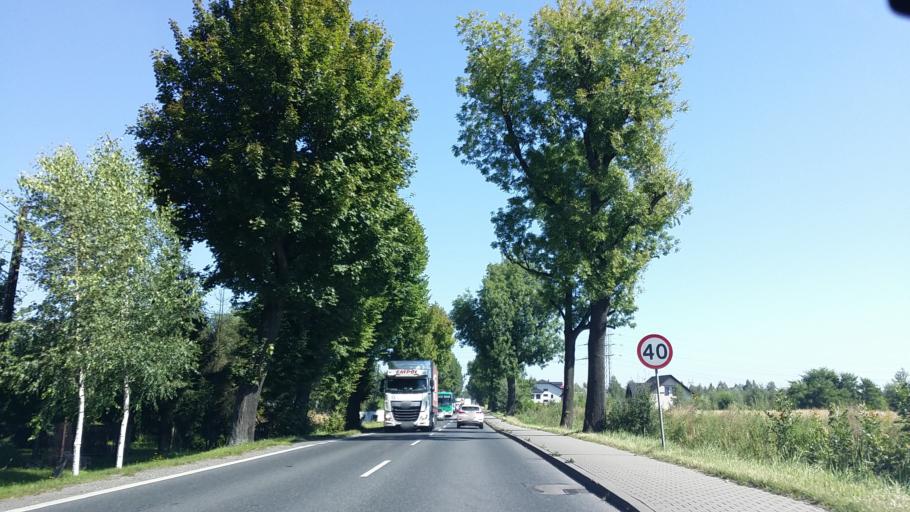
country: PL
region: Lesser Poland Voivodeship
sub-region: Powiat oswiecimski
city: Babice
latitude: 50.0810
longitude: 19.1954
